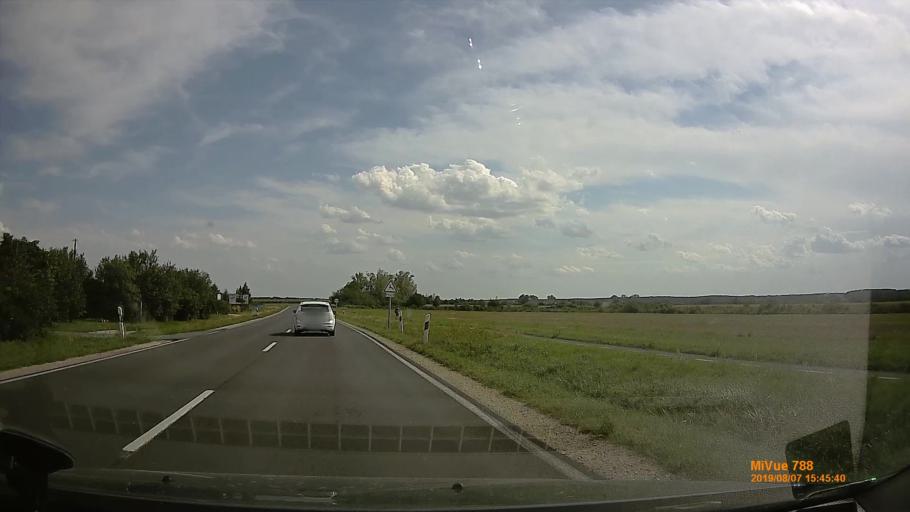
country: HU
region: Vas
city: Szombathely
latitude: 47.1946
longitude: 16.6198
